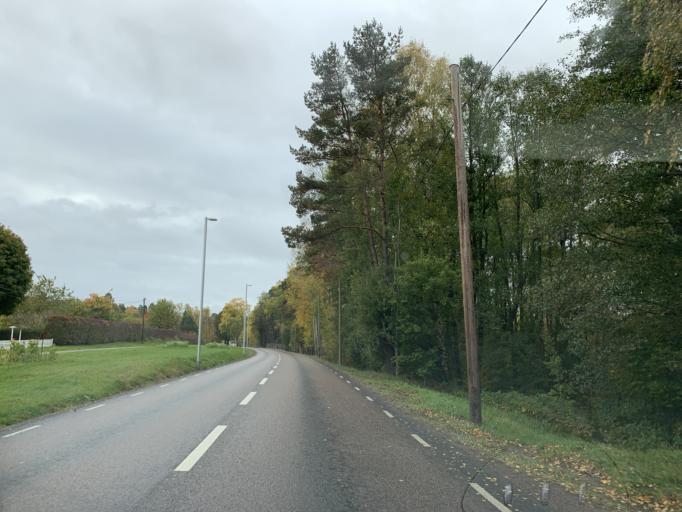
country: SE
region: Stockholm
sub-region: Botkyrka Kommun
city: Varsta
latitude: 59.1696
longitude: 17.7977
